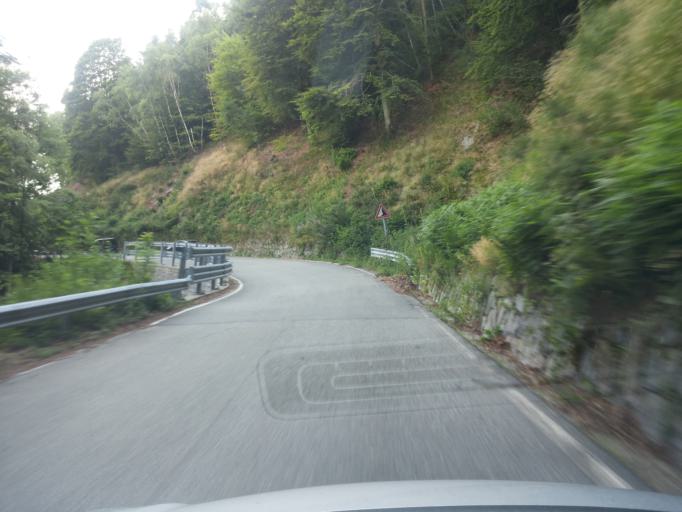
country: IT
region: Piedmont
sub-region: Provincia di Biella
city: Quittengo
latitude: 45.6607
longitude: 8.0214
